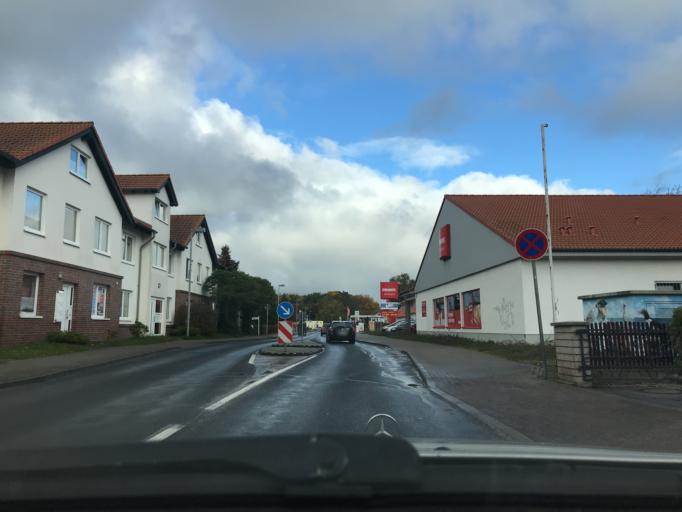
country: DE
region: Mecklenburg-Vorpommern
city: Karlshagen
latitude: 54.1148
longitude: 13.8317
